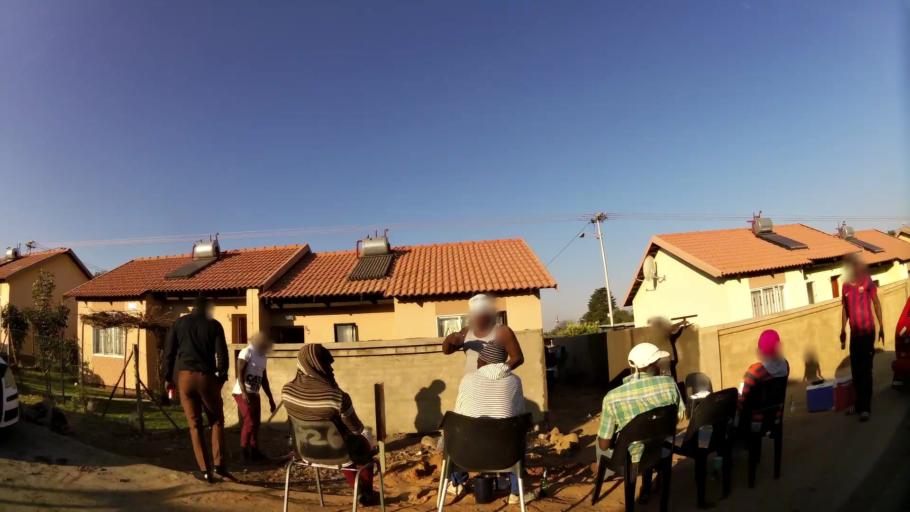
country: ZA
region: Gauteng
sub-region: City of Tshwane Metropolitan Municipality
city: Pretoria
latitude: -25.7409
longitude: 28.1217
